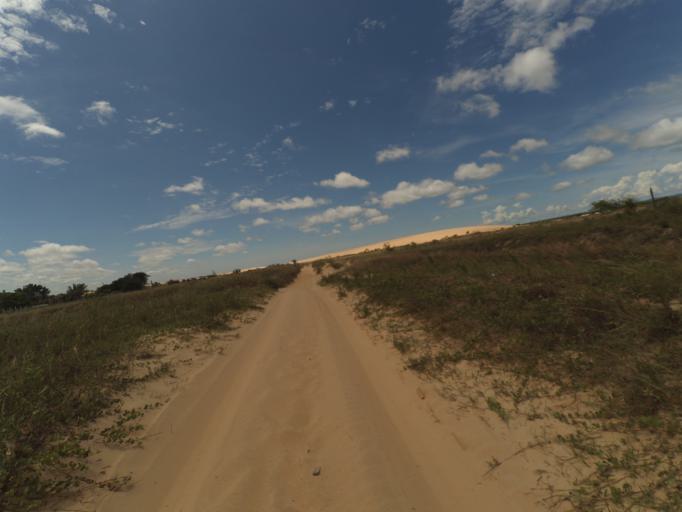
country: BO
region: Santa Cruz
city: Santa Cruz de la Sierra
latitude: -17.9347
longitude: -63.1589
